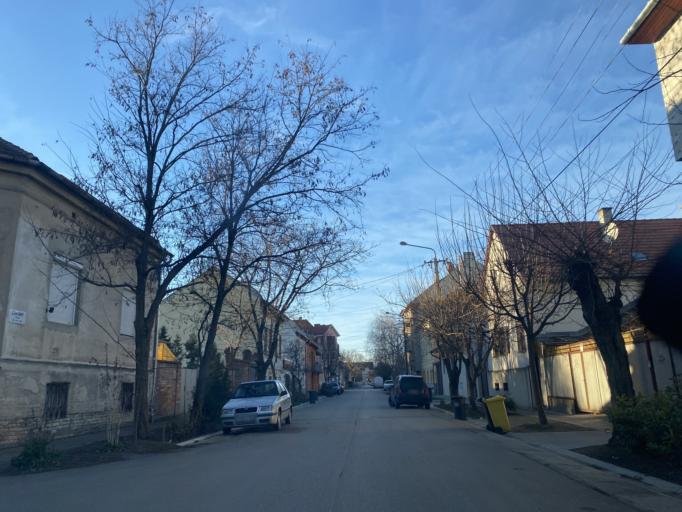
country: HU
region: Csongrad
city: Szeged
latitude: 46.2622
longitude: 20.1419
